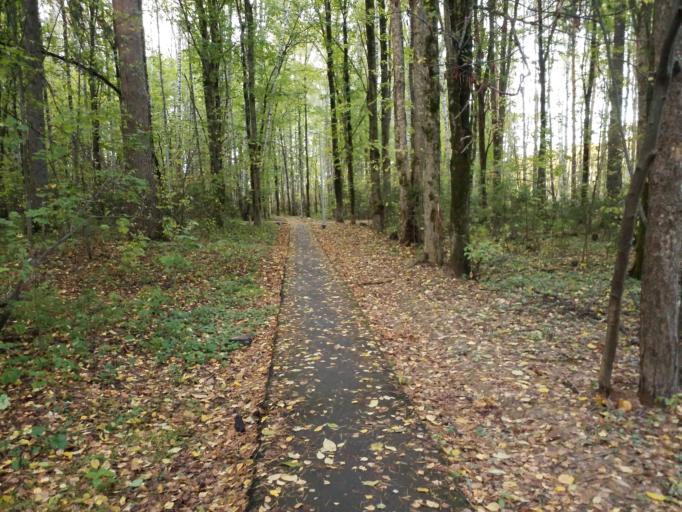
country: RU
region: Moskovskaya
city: Ashukino
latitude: 56.1615
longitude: 37.9585
